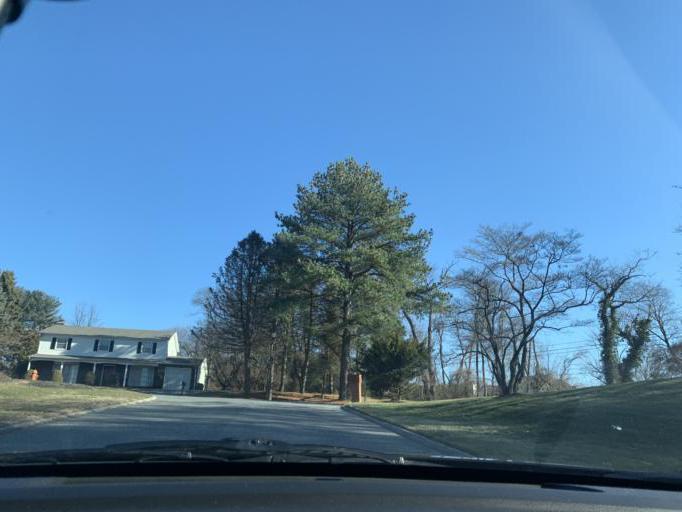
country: US
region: Maryland
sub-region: Baltimore County
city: Garrison
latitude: 39.3926
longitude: -76.7534
